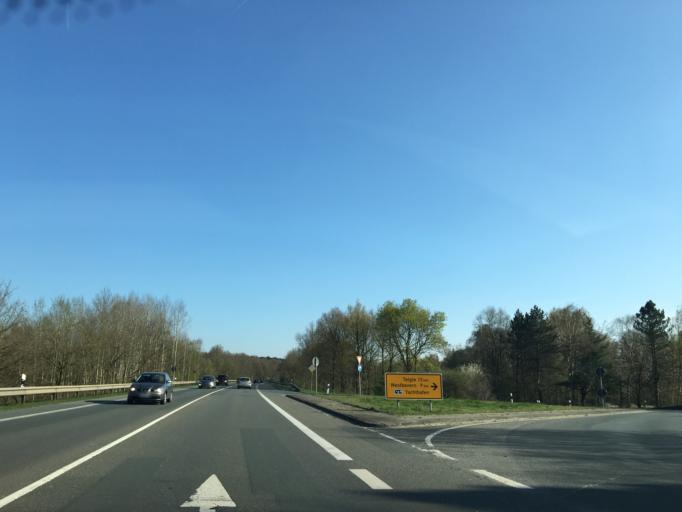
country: DE
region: North Rhine-Westphalia
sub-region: Regierungsbezirk Munster
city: Greven
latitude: 52.0600
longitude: 7.6751
